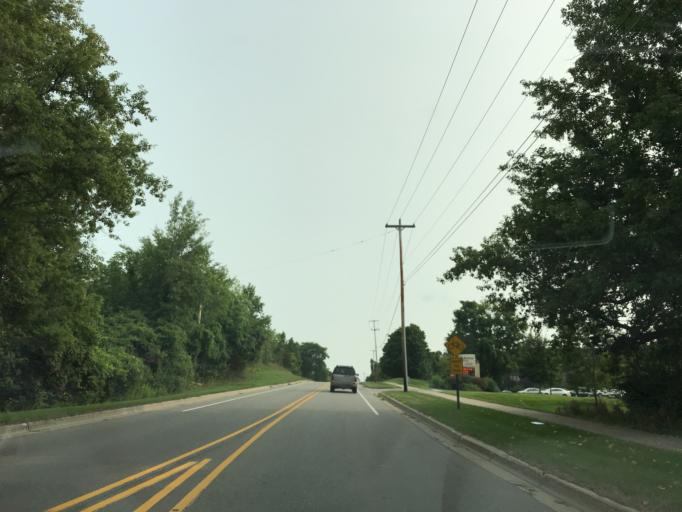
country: US
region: Michigan
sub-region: Ingham County
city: Okemos
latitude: 42.7449
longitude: -84.4475
